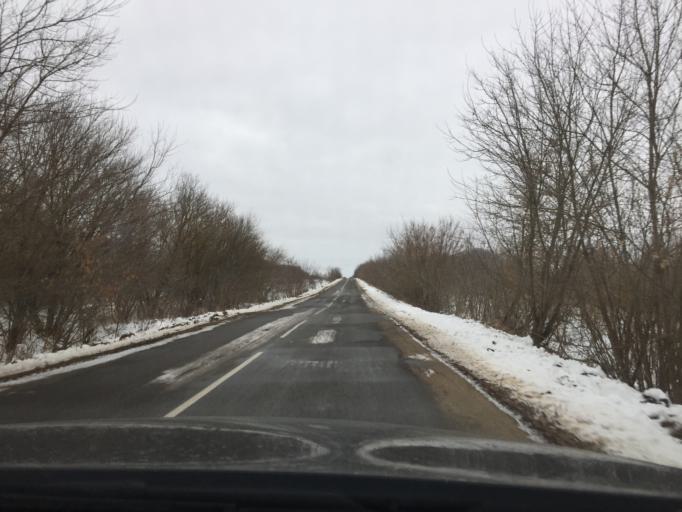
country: RU
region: Tula
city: Teploye
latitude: 53.7932
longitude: 37.6044
